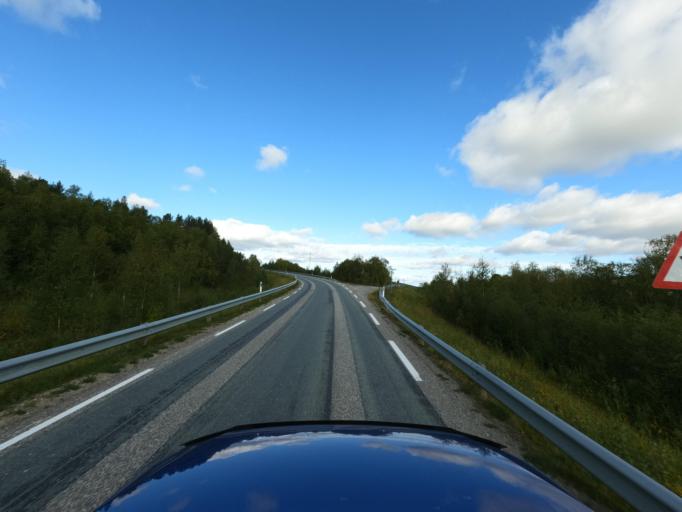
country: NO
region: Finnmark Fylke
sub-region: Karasjok
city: Karasjohka
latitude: 69.4278
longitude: 25.7942
